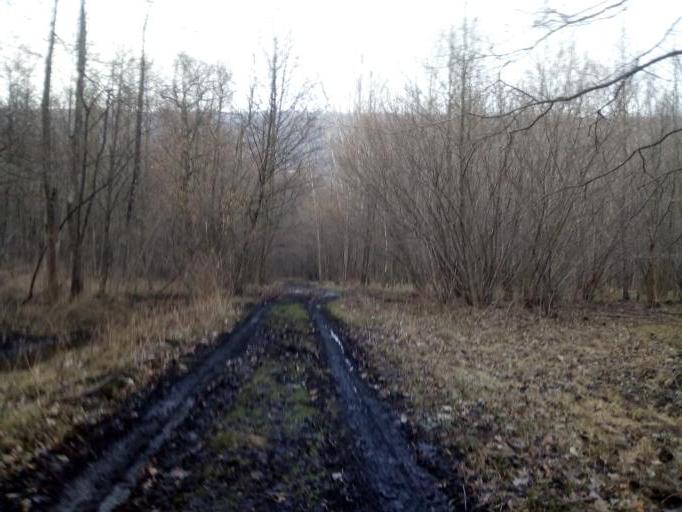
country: IT
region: Piedmont
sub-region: Provincia di Torino
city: Cascinette d'Ivrea
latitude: 45.4912
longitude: 7.9155
